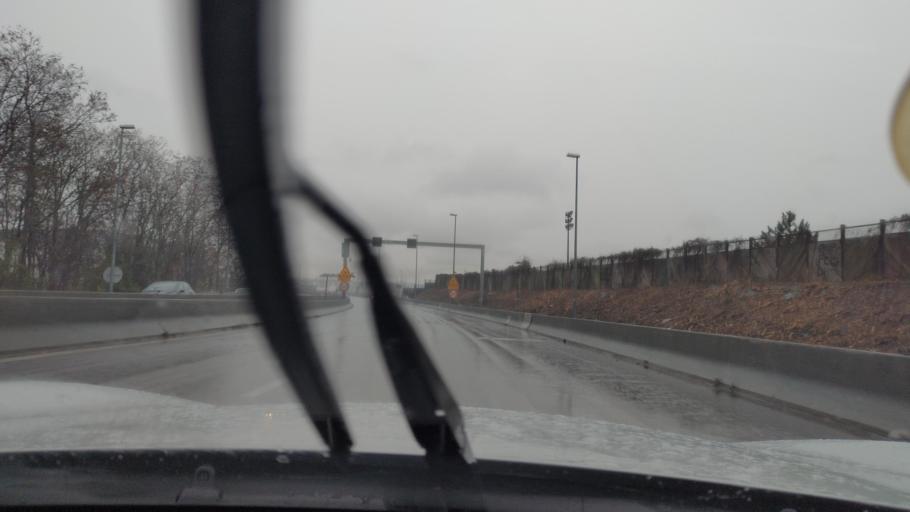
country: FR
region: Ile-de-France
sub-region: Departement de Seine-Saint-Denis
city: La Courneuve
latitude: 48.9300
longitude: 2.4028
